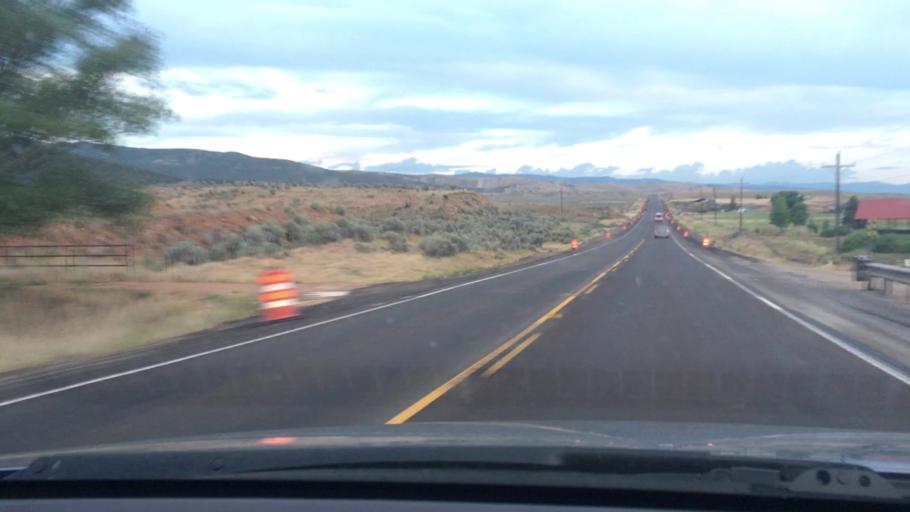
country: US
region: Utah
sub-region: Utah County
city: Woodland Hills
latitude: 39.8646
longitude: -111.5304
